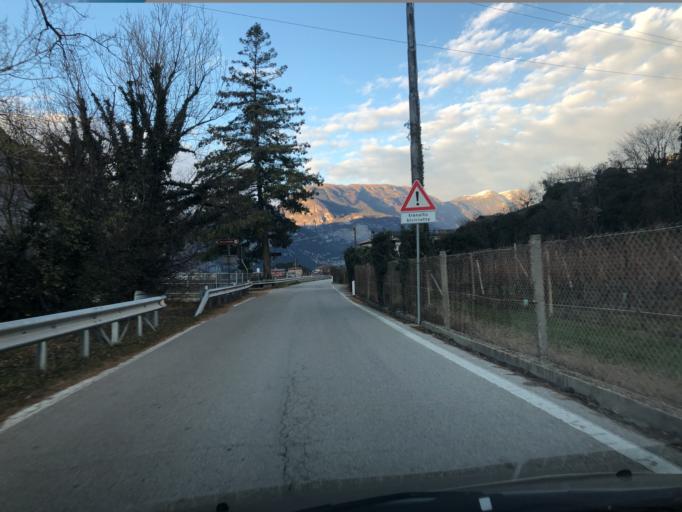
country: IT
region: Trentino-Alto Adige
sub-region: Provincia di Trento
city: Pietramurata
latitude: 46.0104
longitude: 10.9569
